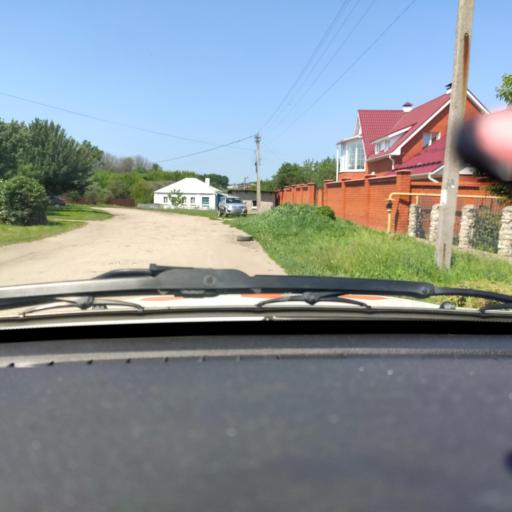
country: RU
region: Voronezj
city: Devitsa
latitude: 51.5964
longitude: 38.9862
